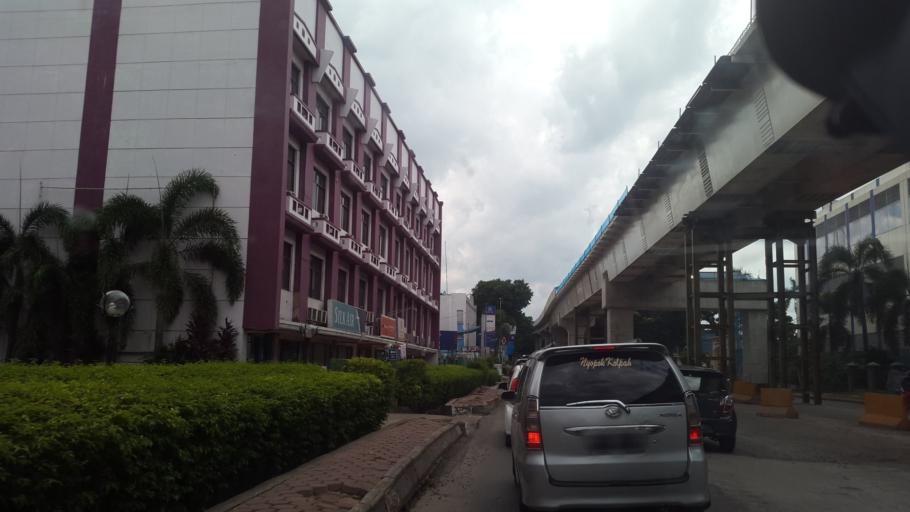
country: ID
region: South Sumatra
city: Plaju
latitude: -2.9774
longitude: 104.7522
